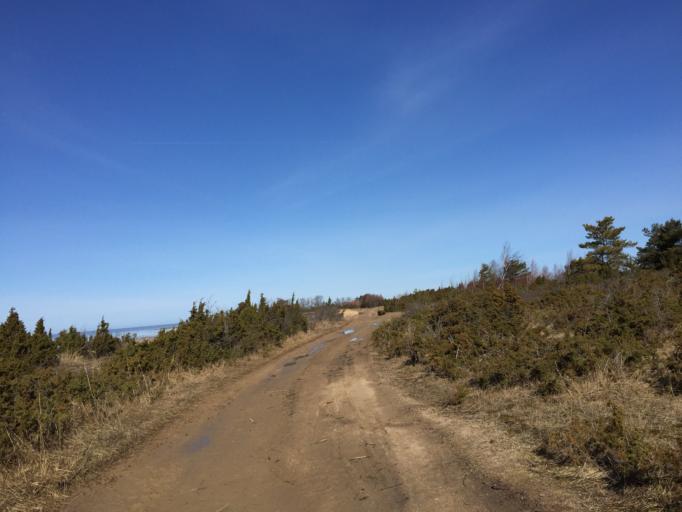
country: EE
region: Laeaene
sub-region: Haapsalu linn
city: Haapsalu
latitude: 58.6502
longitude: 23.5068
